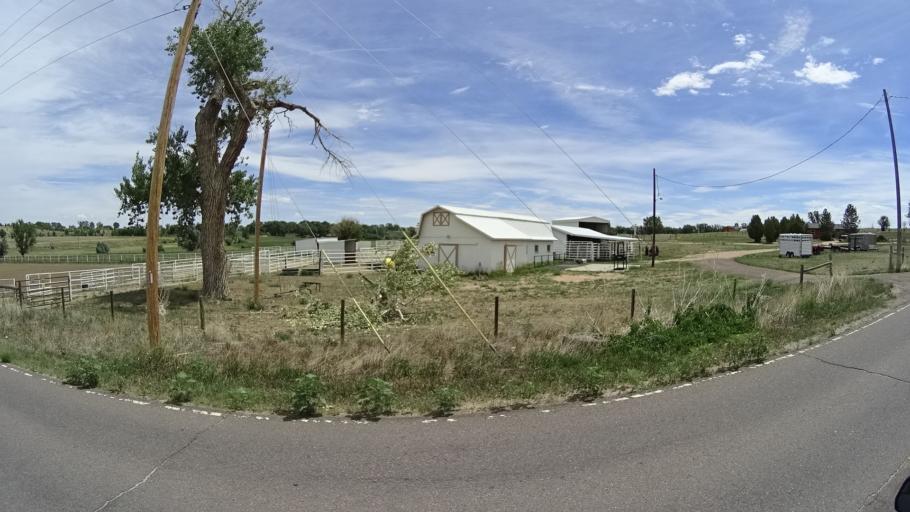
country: US
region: Colorado
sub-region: El Paso County
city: Fountain
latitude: 38.6847
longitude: -104.6737
